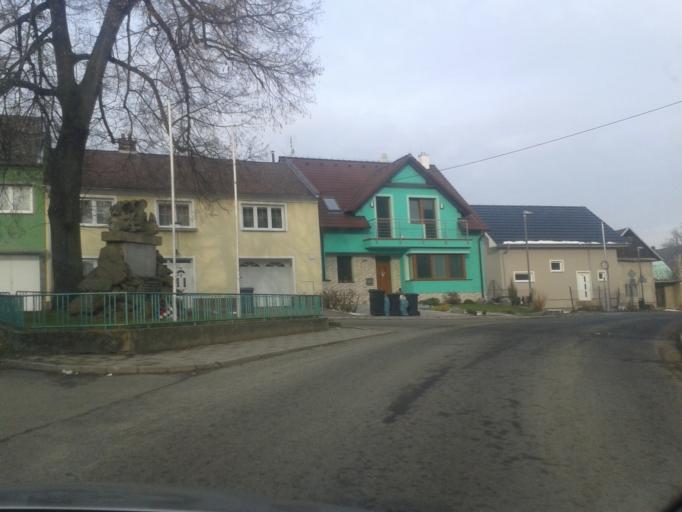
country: CZ
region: Olomoucky
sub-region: Okres Olomouc
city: Slatinice
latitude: 49.5477
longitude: 17.0942
